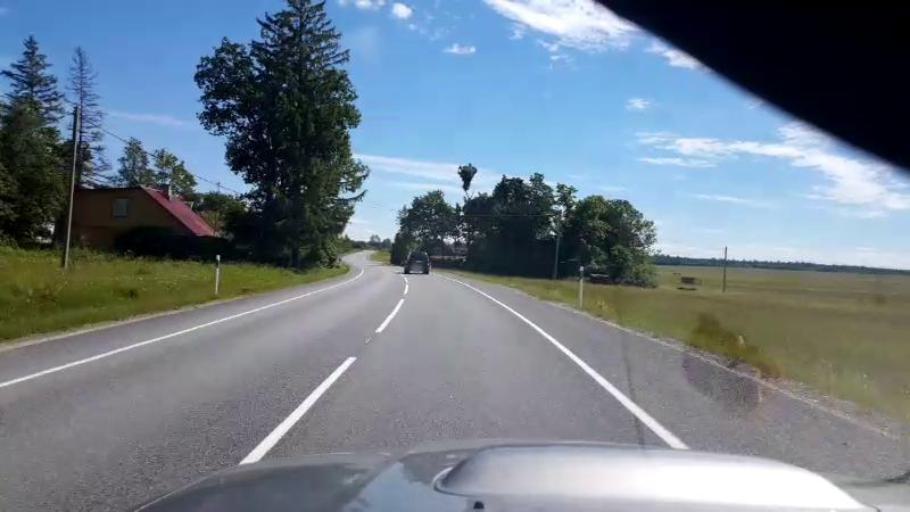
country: EE
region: Jaervamaa
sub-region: Jaerva-Jaani vald
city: Jarva-Jaani
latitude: 59.0237
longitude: 25.8980
